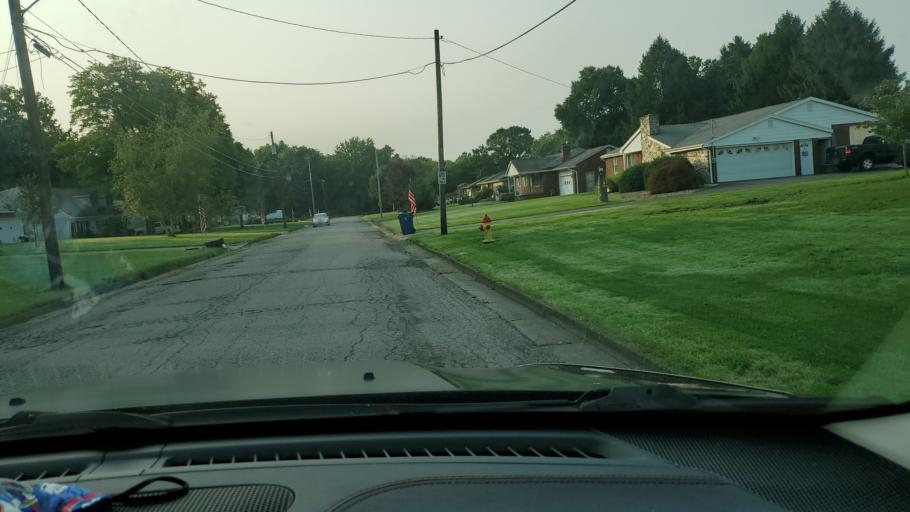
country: US
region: Ohio
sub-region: Mahoning County
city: Struthers
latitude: 41.0378
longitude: -80.6019
